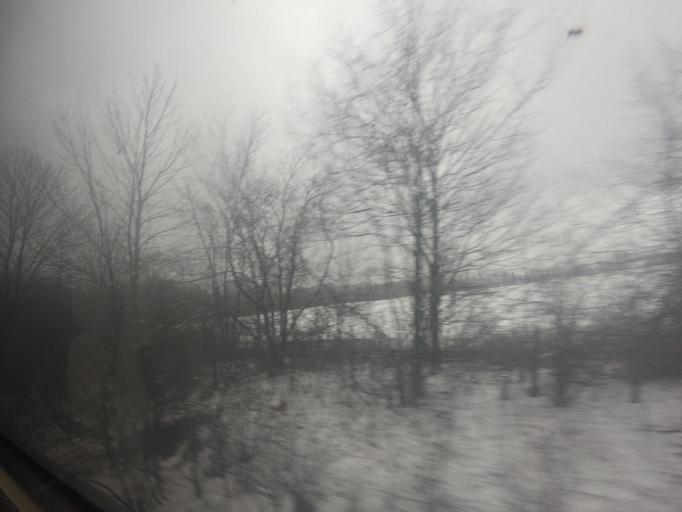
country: CA
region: Ontario
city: Cobourg
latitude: 43.9248
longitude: -78.4257
